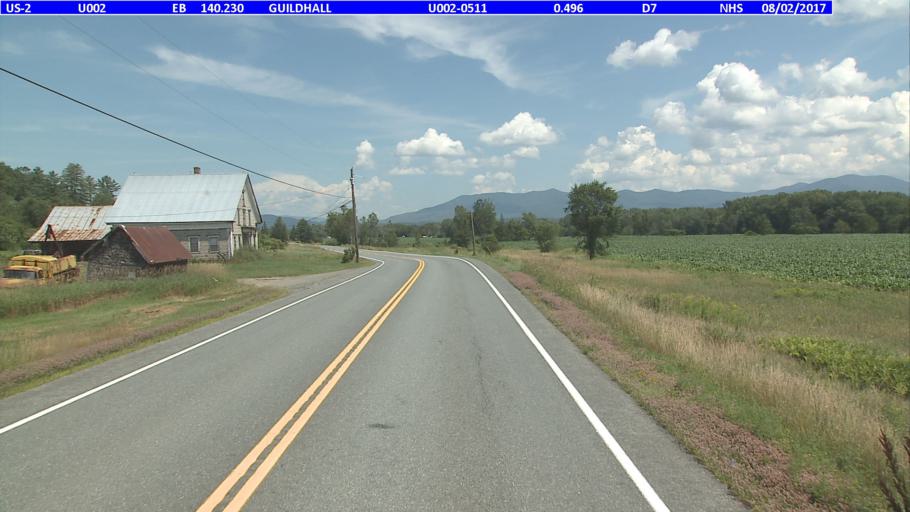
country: US
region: New Hampshire
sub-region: Coos County
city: Lancaster
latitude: 44.4889
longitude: -71.6018
